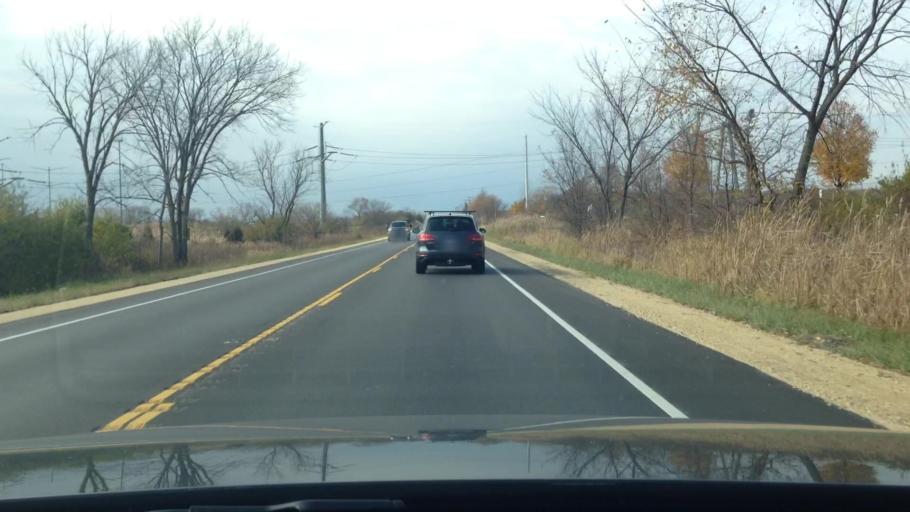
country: US
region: Illinois
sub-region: McHenry County
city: Woodstock
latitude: 42.2551
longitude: -88.4383
